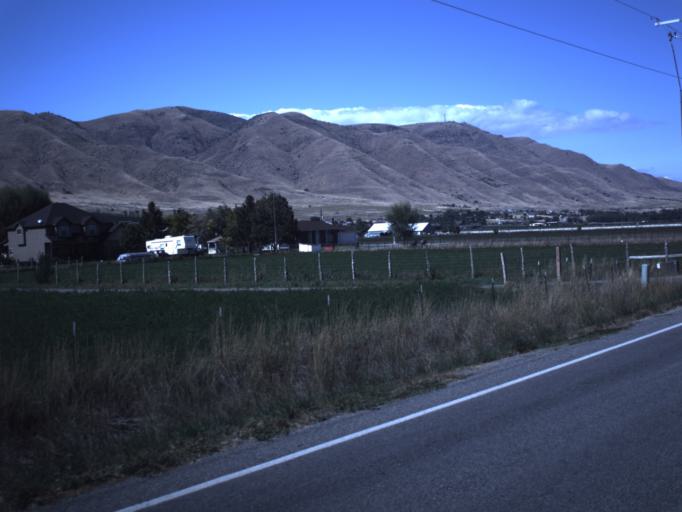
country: US
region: Utah
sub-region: Utah County
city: West Mountain
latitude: 40.0440
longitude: -111.7873
